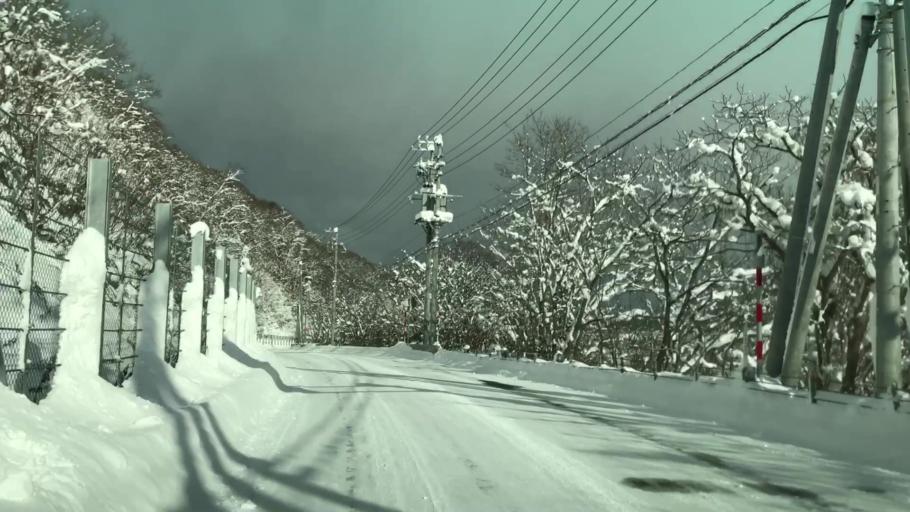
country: JP
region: Hokkaido
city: Yoichi
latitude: 43.2937
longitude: 140.5928
